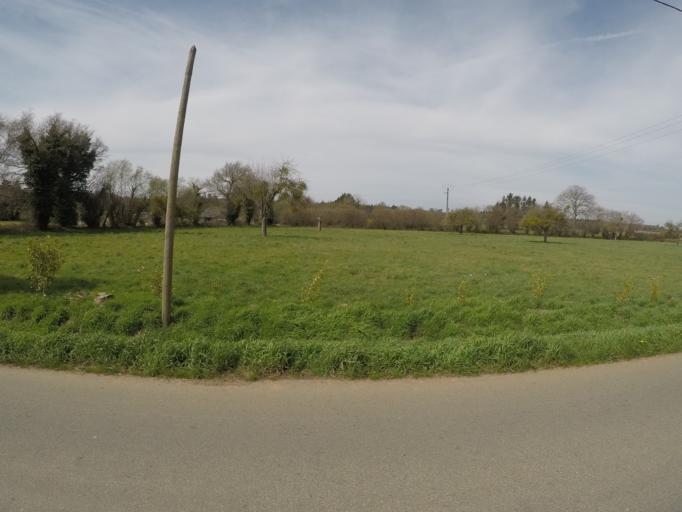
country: FR
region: Brittany
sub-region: Departement des Cotes-d'Armor
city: Plelo
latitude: 48.5713
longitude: -2.9258
